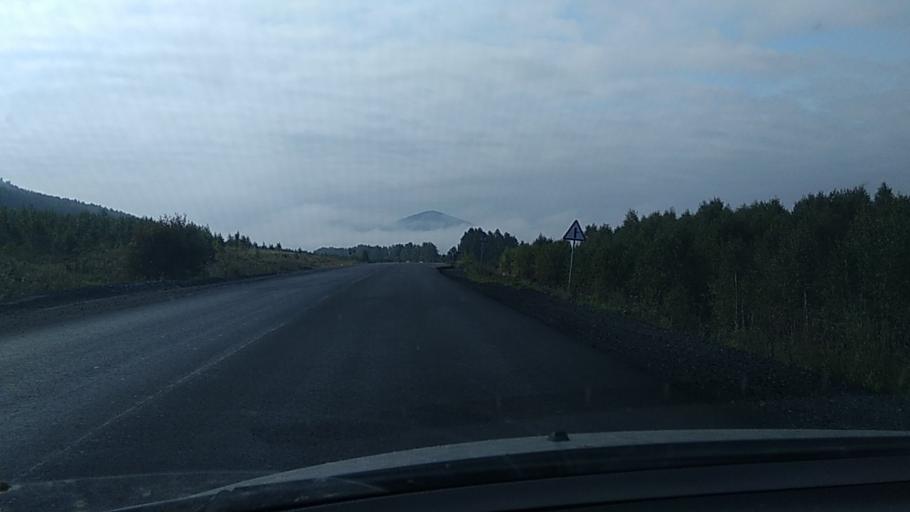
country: RU
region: Chelyabinsk
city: Karabash
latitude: 55.3633
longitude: 60.2447
